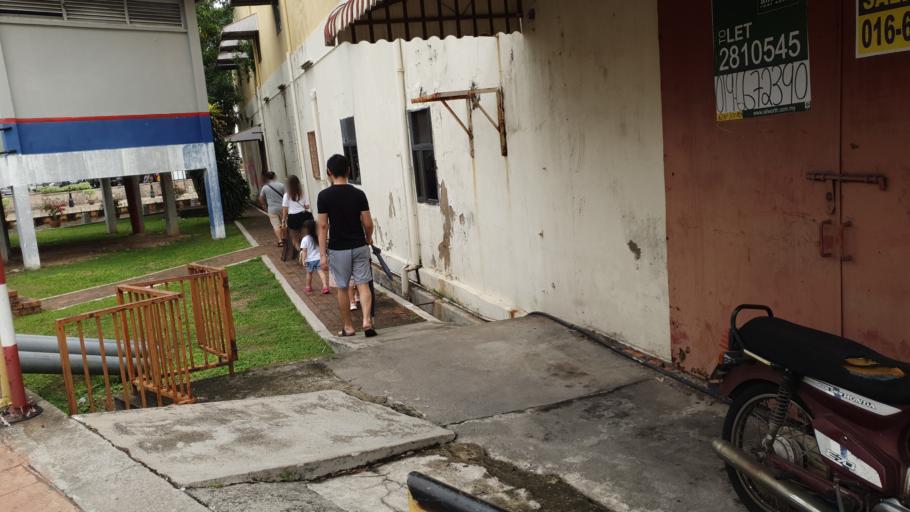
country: MY
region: Melaka
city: Malacca
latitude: 2.1964
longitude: 102.2502
